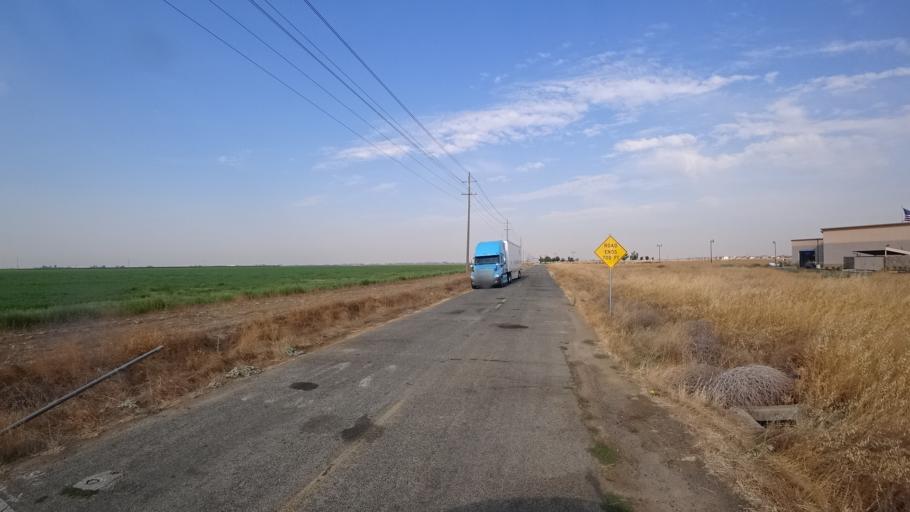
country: US
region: California
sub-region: Sacramento County
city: Elk Grove
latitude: 38.3727
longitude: -121.3652
